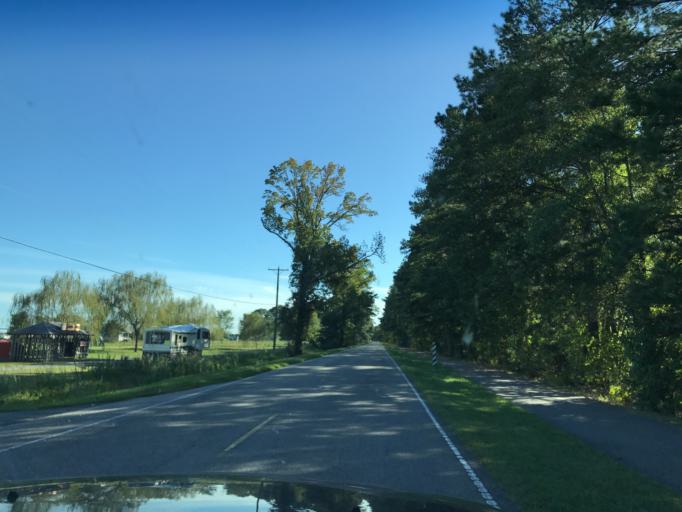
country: US
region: Virginia
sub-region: City of Portsmouth
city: Portsmouth Heights
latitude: 36.7134
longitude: -76.3525
